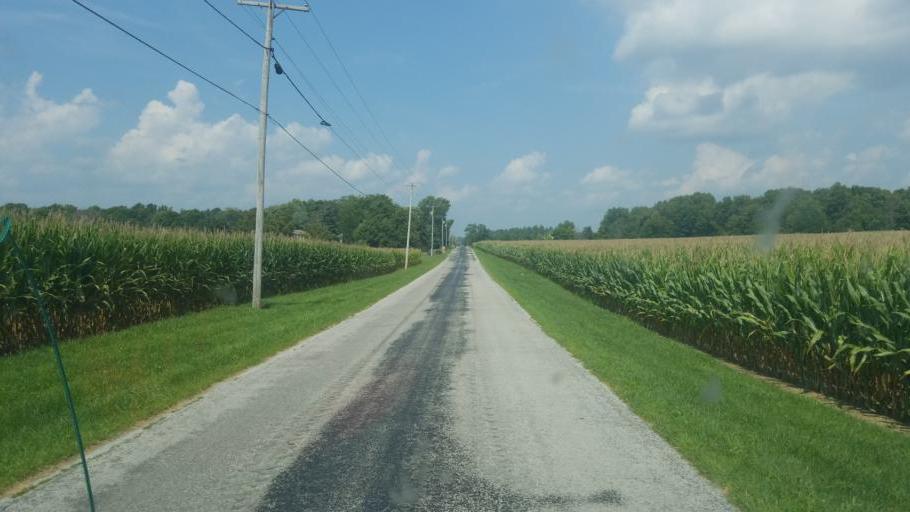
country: US
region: Ohio
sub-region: Richland County
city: Shelby
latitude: 40.8746
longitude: -82.5956
